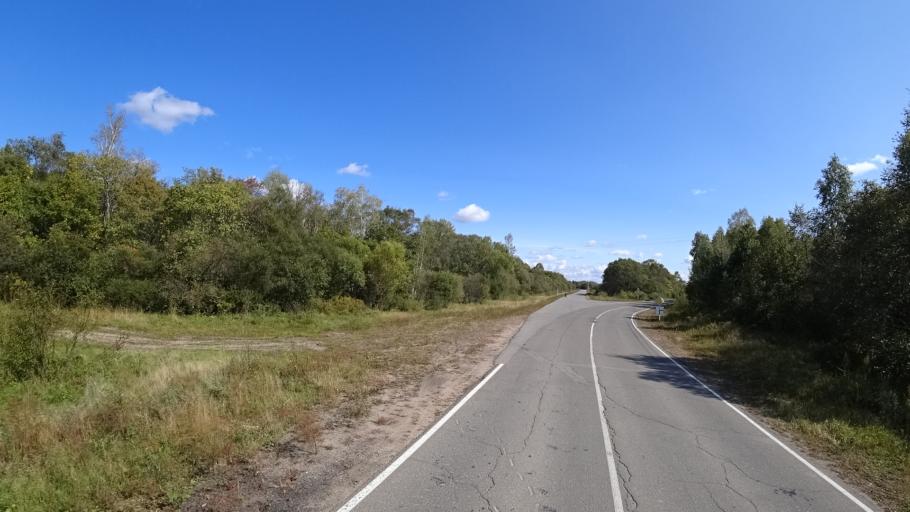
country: RU
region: Amur
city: Arkhara
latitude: 49.4060
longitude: 130.1249
